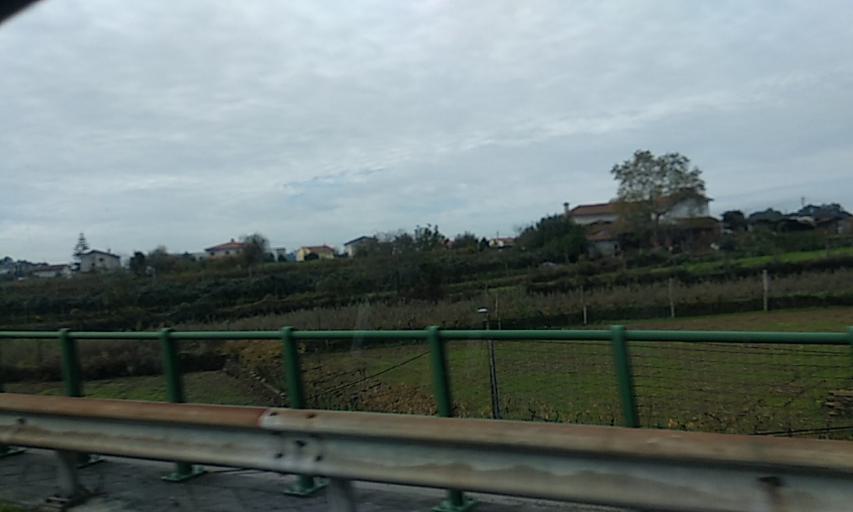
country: PT
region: Porto
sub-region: Santo Tirso
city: Santo Tirso
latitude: 41.3459
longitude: -8.5057
